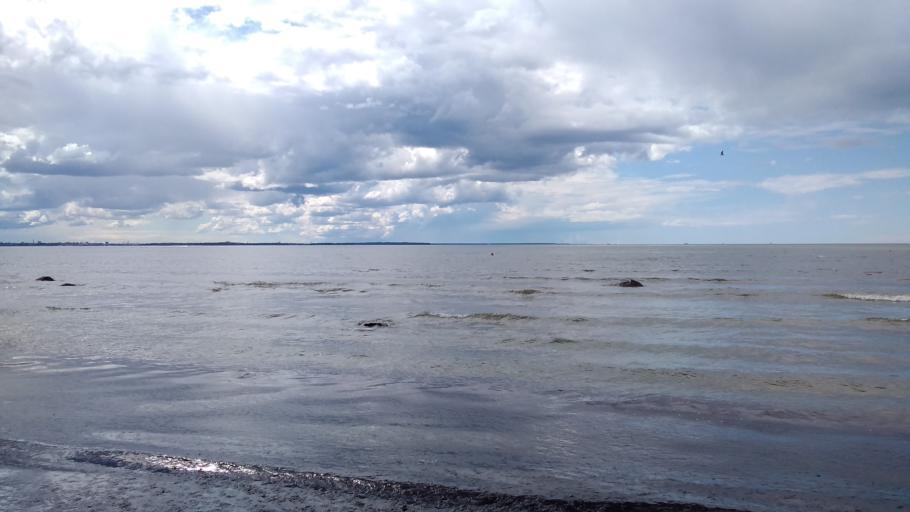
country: EE
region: Harju
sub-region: Viimsi vald
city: Haabneeme
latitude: 59.5120
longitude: 24.8143
